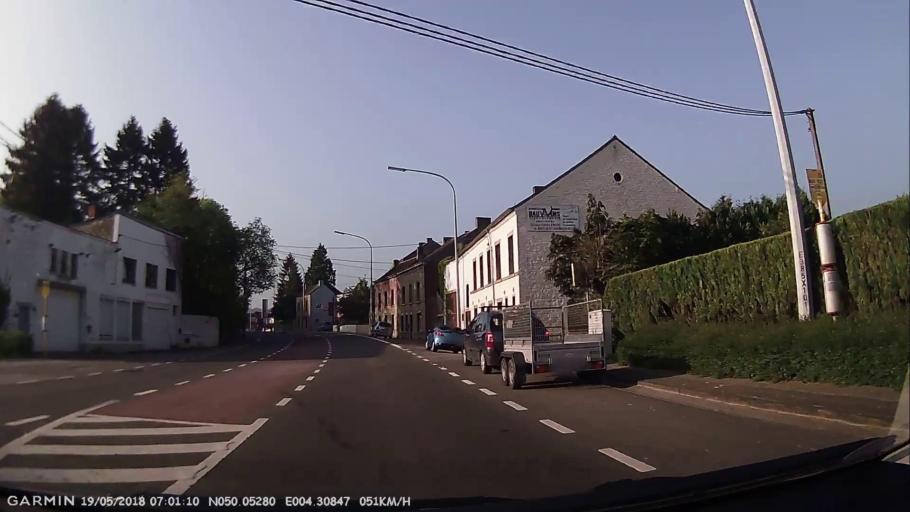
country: BE
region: Wallonia
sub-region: Province du Hainaut
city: Chimay
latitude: 50.0527
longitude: 4.3085
